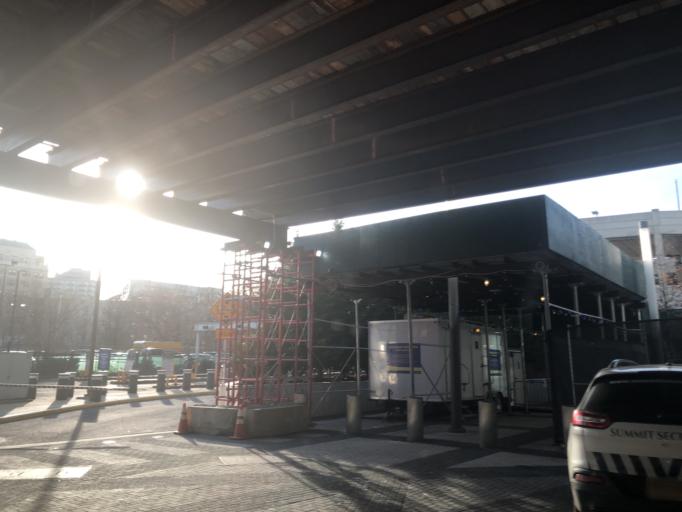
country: US
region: New Jersey
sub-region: Hudson County
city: Jersey City
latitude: 40.7319
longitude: -74.0605
